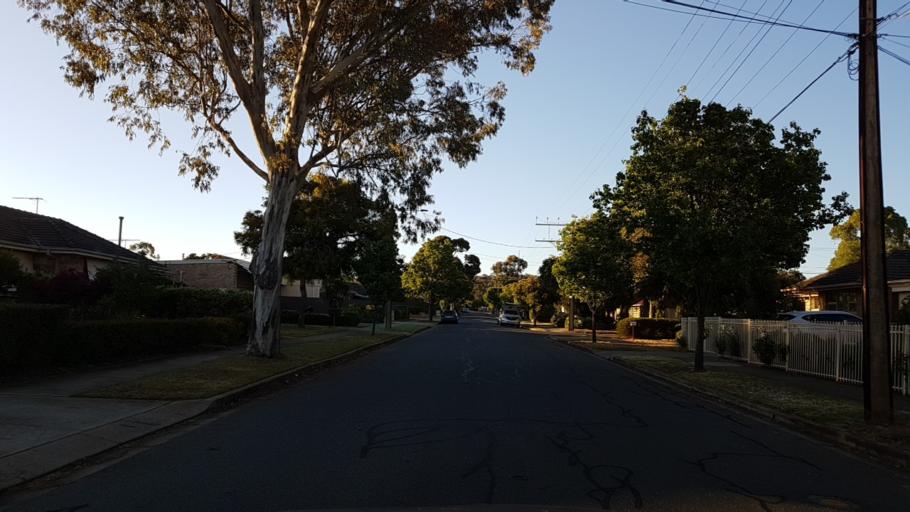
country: AU
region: South Australia
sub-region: Marion
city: Sturt
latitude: -35.0193
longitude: 138.5528
